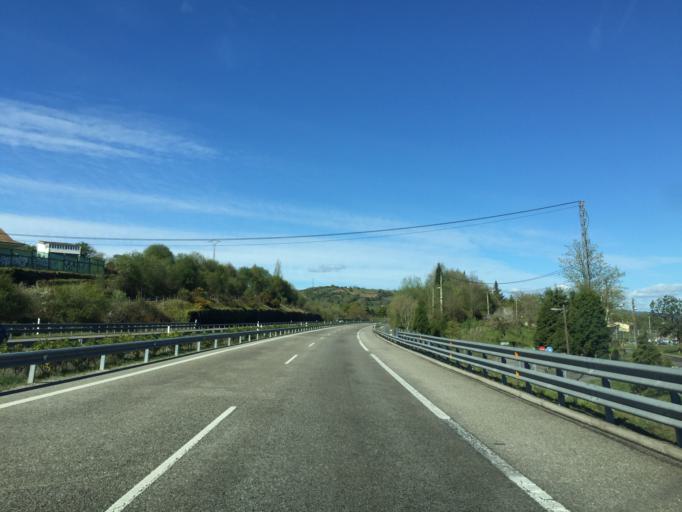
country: ES
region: Asturias
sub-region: Province of Asturias
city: Castandiello
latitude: 43.3526
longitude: -5.9268
